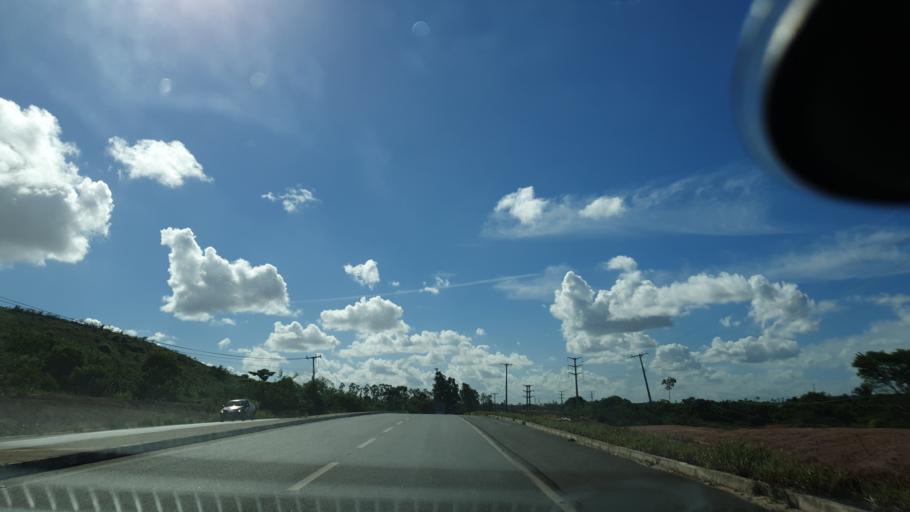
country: BR
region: Bahia
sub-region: Camacari
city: Camacari
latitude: -12.6852
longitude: -38.2577
